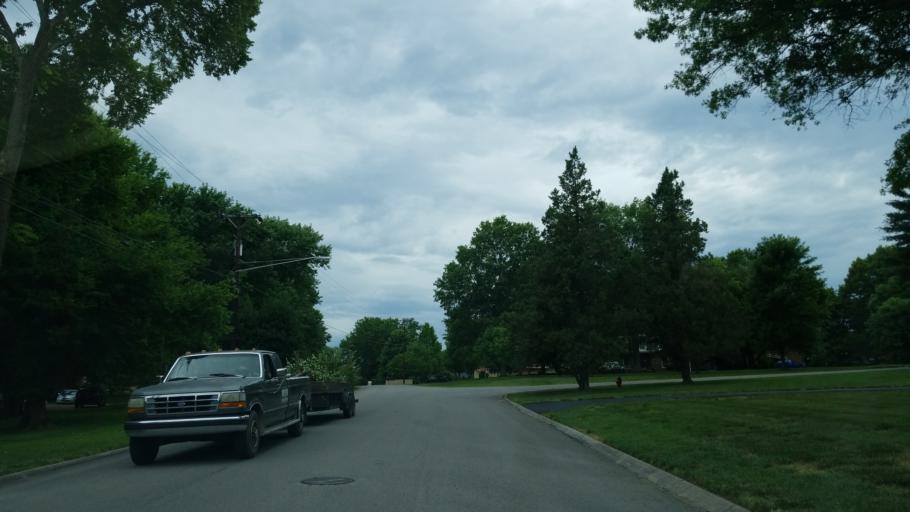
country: US
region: Tennessee
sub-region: Williamson County
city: Brentwood
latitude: 36.0284
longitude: -86.8229
